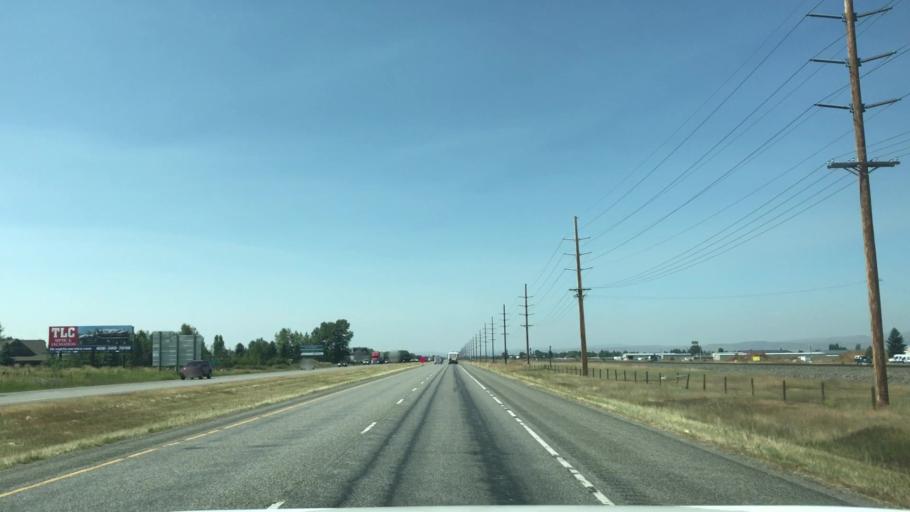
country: US
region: Montana
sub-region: Gallatin County
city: Belgrade
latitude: 45.7920
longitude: -111.2103
